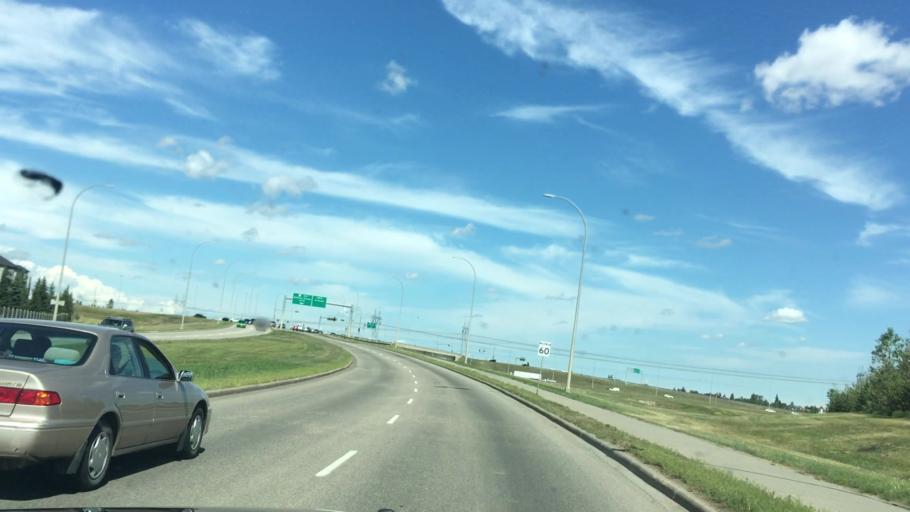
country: CA
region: Alberta
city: Beaumont
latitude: 53.4303
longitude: -113.5167
